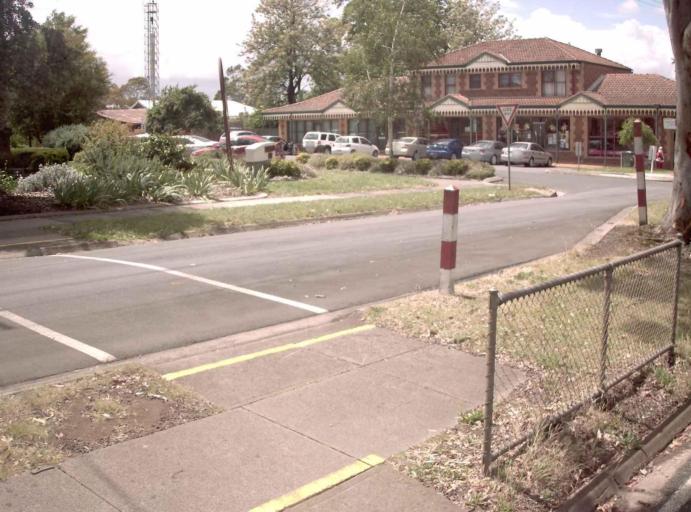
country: AU
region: Victoria
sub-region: Baw Baw
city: Warragul
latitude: -38.1331
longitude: 145.8537
